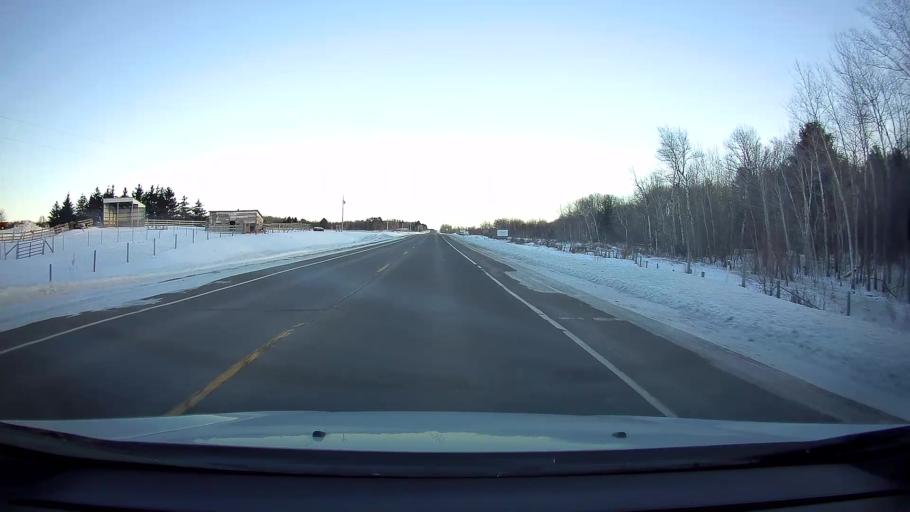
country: US
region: Wisconsin
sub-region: Barron County
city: Cumberland
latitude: 45.6136
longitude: -92.0077
